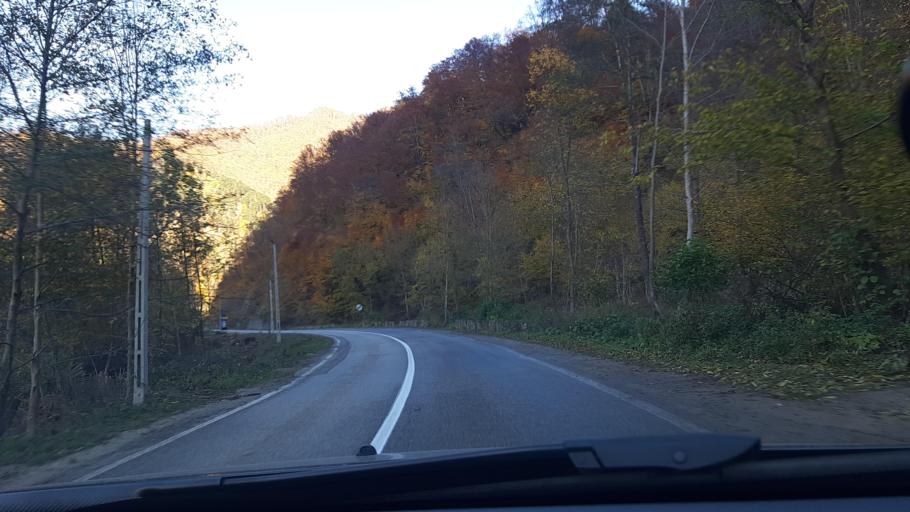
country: RO
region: Valcea
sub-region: Comuna Brezoi
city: Brezoi
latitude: 45.3476
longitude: 24.1501
